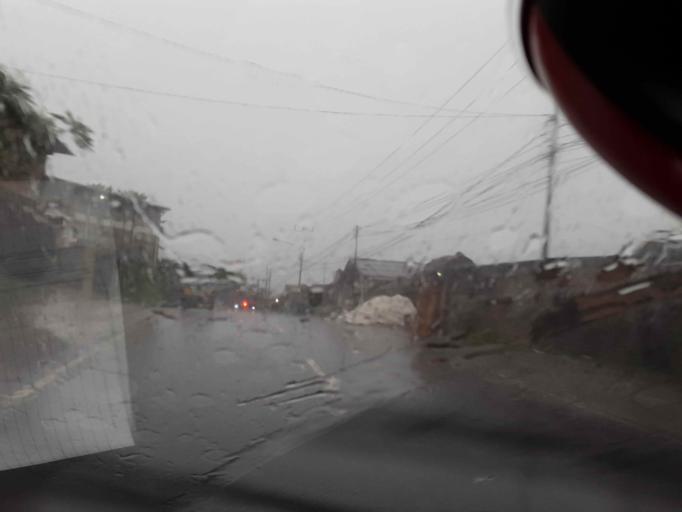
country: ID
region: West Java
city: Cimahi
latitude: -6.8774
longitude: 107.5042
